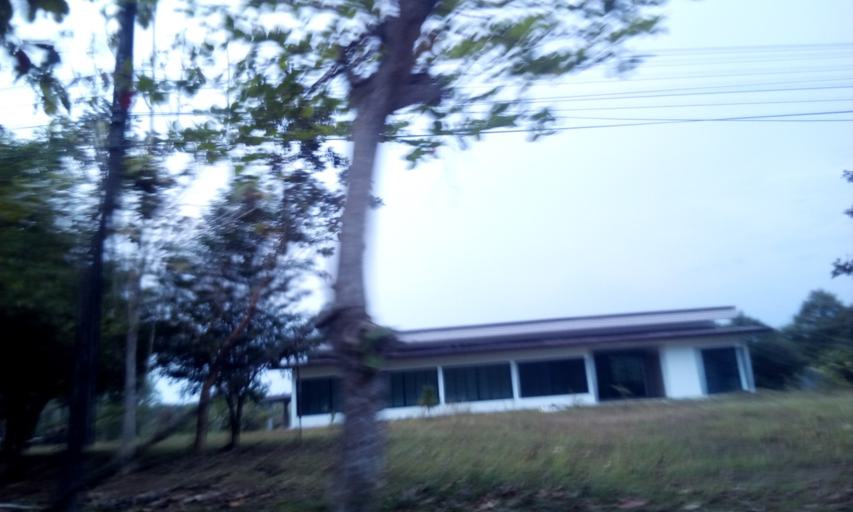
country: TH
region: Trat
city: Khao Saming
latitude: 12.3257
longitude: 102.3677
